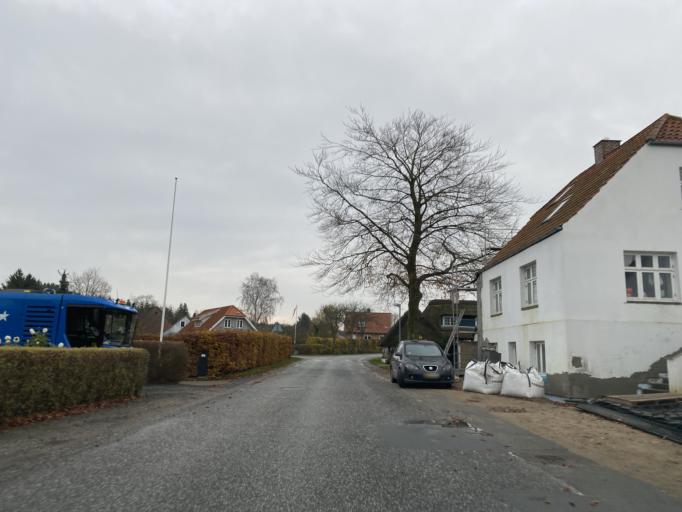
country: DK
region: Central Jutland
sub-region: Silkeborg Kommune
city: Svejbaek
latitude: 56.1536
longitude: 9.6922
